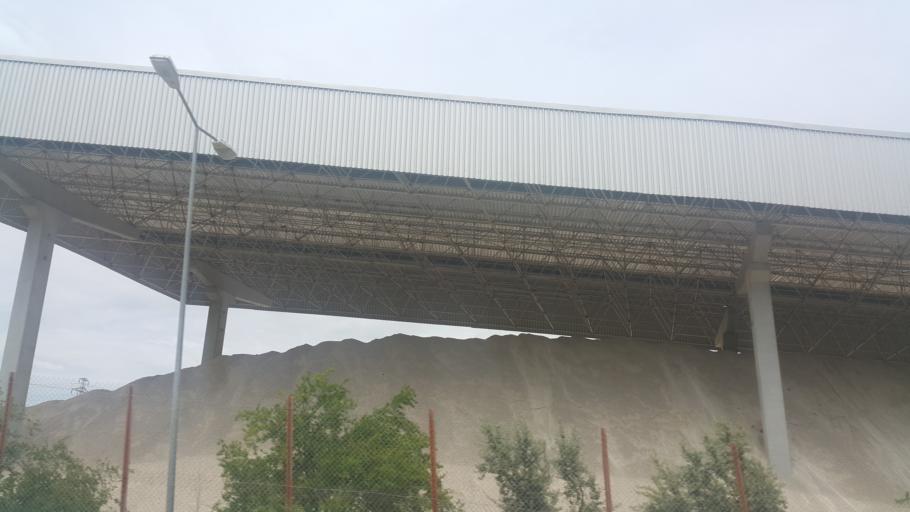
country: TR
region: Adana
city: Ceyhan
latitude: 37.0528
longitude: 35.7811
